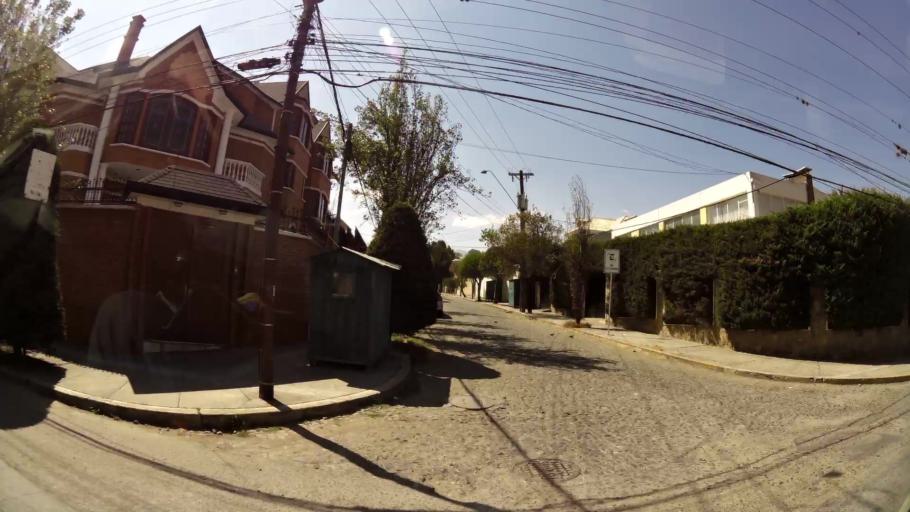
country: BO
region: La Paz
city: La Paz
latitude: -16.5421
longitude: -68.0833
